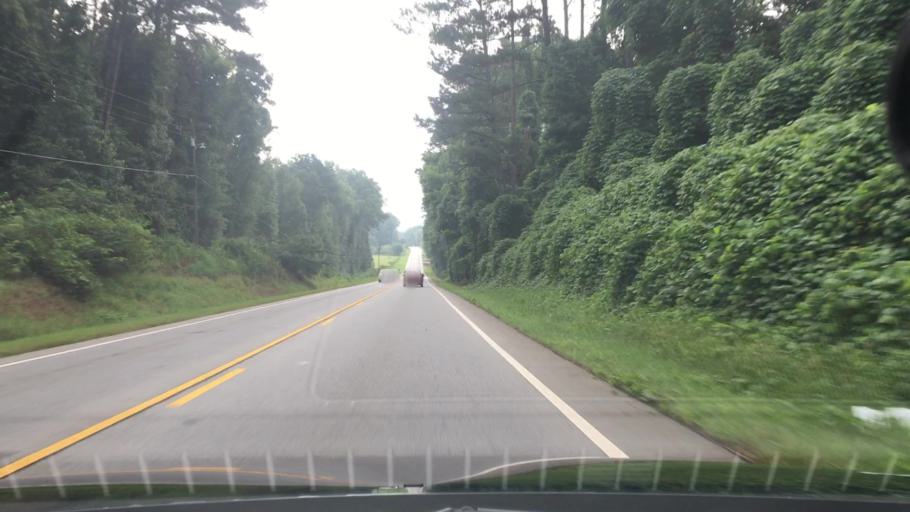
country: US
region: Georgia
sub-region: Spalding County
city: Experiment
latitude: 33.2406
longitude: -84.3395
